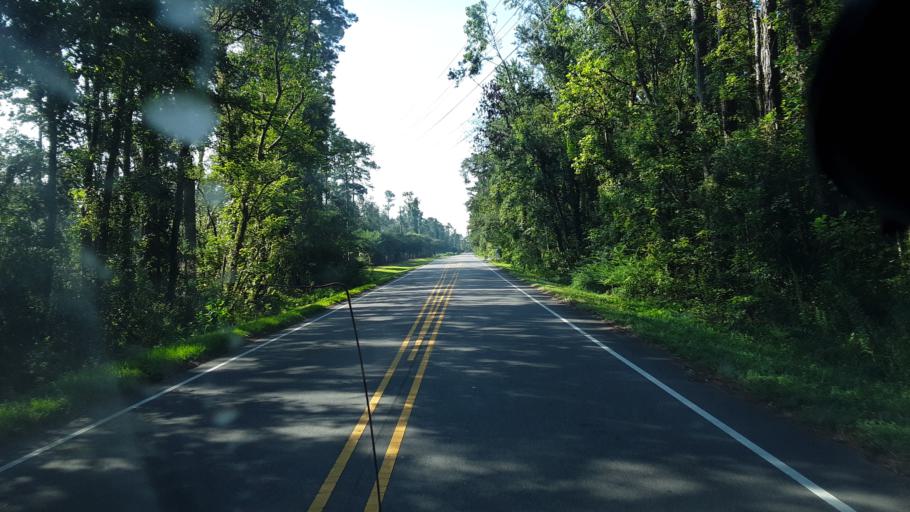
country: US
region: North Carolina
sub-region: Brunswick County
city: Belville
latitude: 34.2086
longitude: -77.9825
